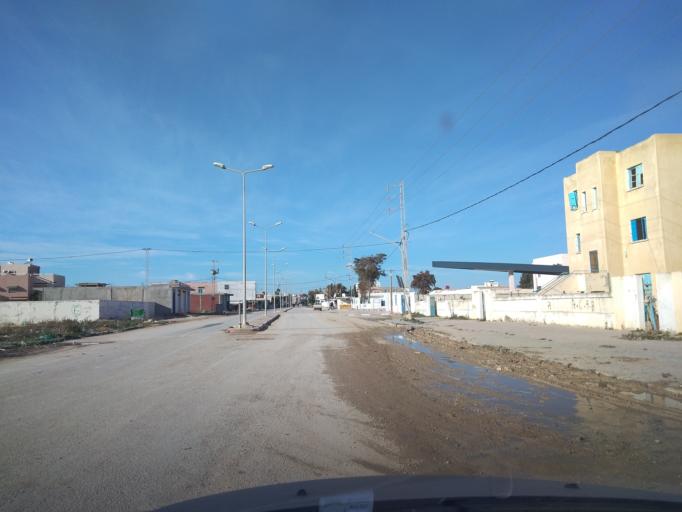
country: TN
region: Ariana
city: Qal'at al Andalus
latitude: 37.0524
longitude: 10.1225
